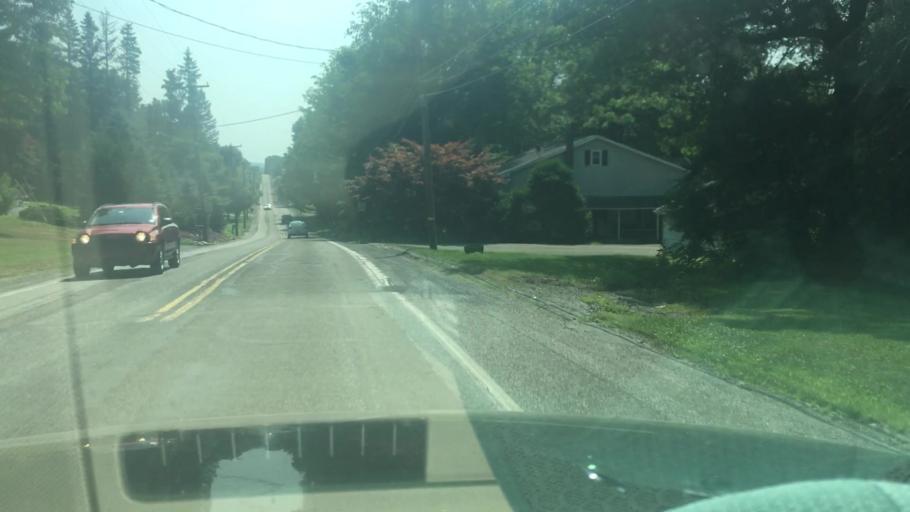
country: US
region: Pennsylvania
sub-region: Schuylkill County
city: Mahanoy City
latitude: 40.8190
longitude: -76.0757
